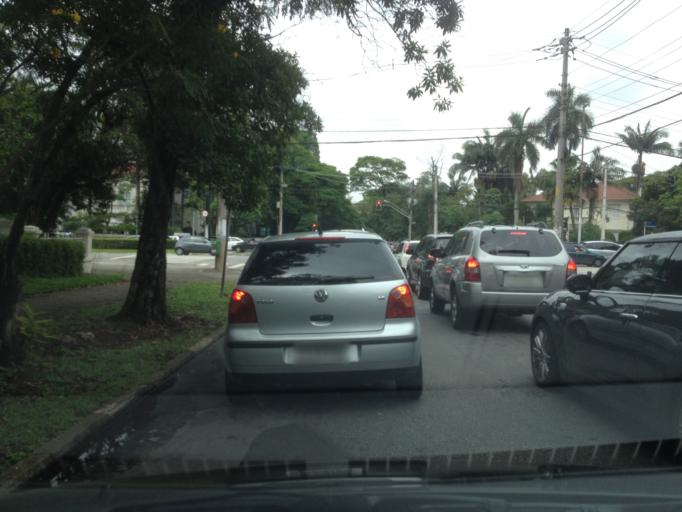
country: BR
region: Sao Paulo
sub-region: Sao Paulo
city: Sao Paulo
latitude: -23.5663
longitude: -46.6745
